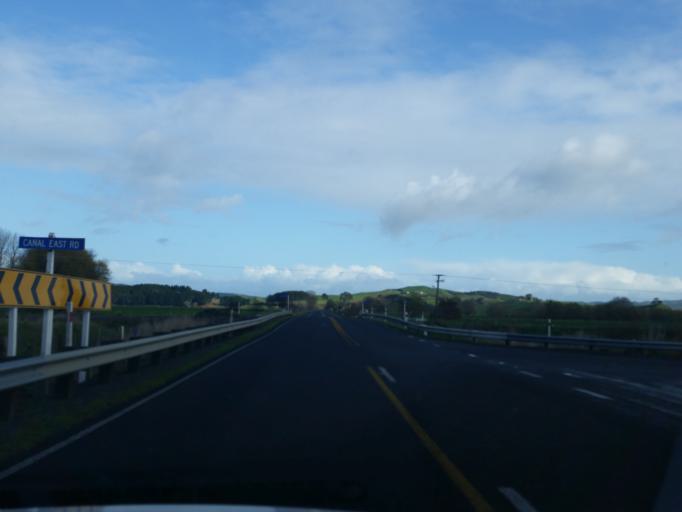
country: NZ
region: Waikato
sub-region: Hauraki District
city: Ngatea
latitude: -37.2805
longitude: 175.4218
